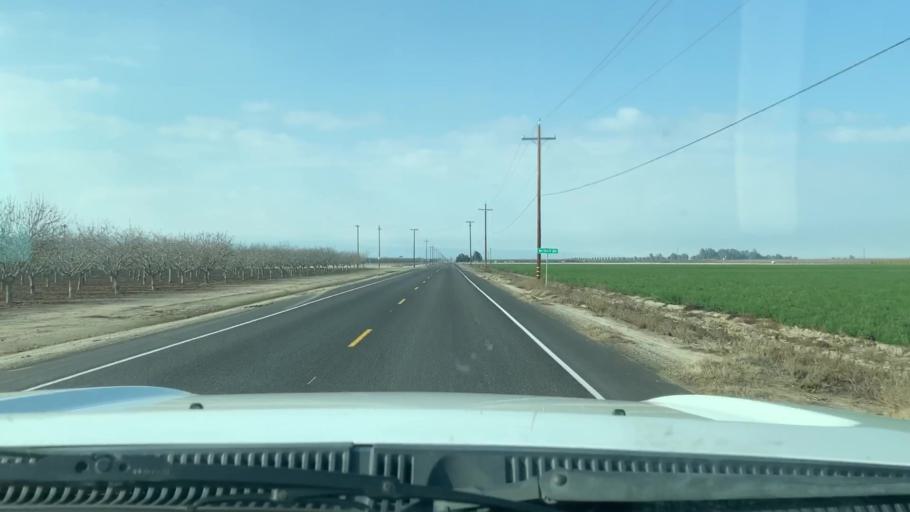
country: US
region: California
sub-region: Kern County
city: Buttonwillow
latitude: 35.4422
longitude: -119.4093
